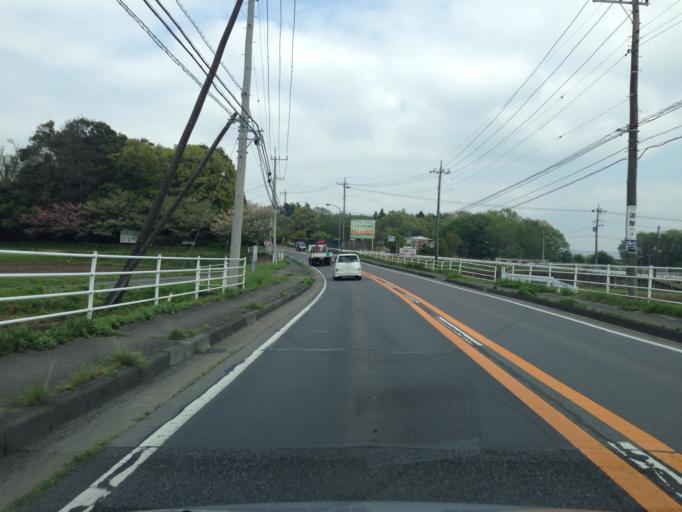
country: JP
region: Ibaraki
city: Iwase
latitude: 36.3428
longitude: 140.0395
